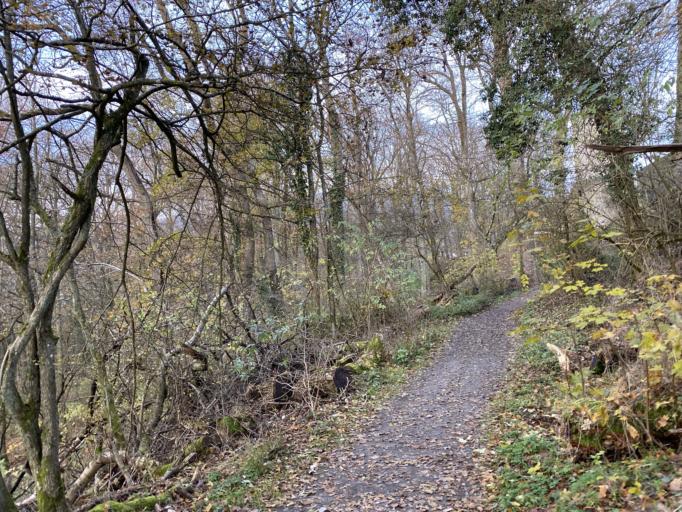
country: DE
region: Hesse
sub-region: Regierungsbezirk Darmstadt
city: Konigstein im Taunus
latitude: 50.1896
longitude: 8.4756
